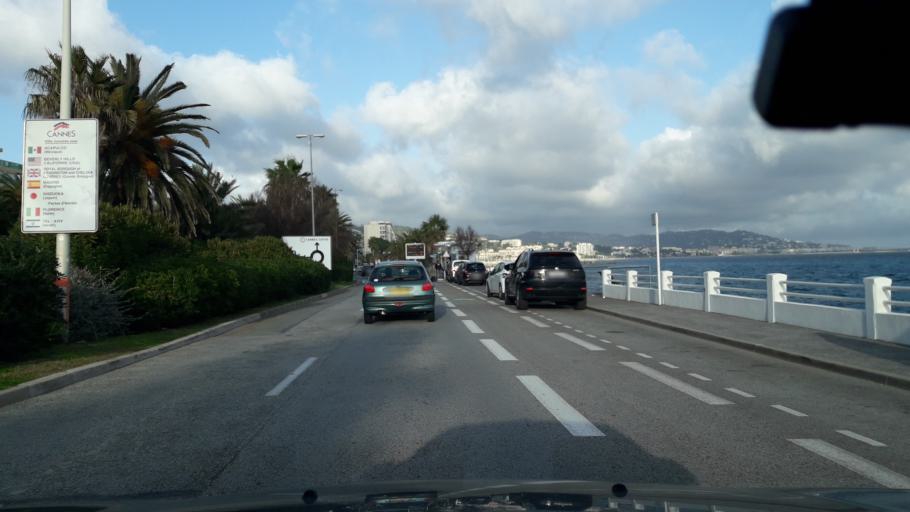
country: FR
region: Provence-Alpes-Cote d'Azur
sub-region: Departement des Alpes-Maritimes
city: Mandelieu-la-Napoule
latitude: 43.5405
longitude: 6.9596
